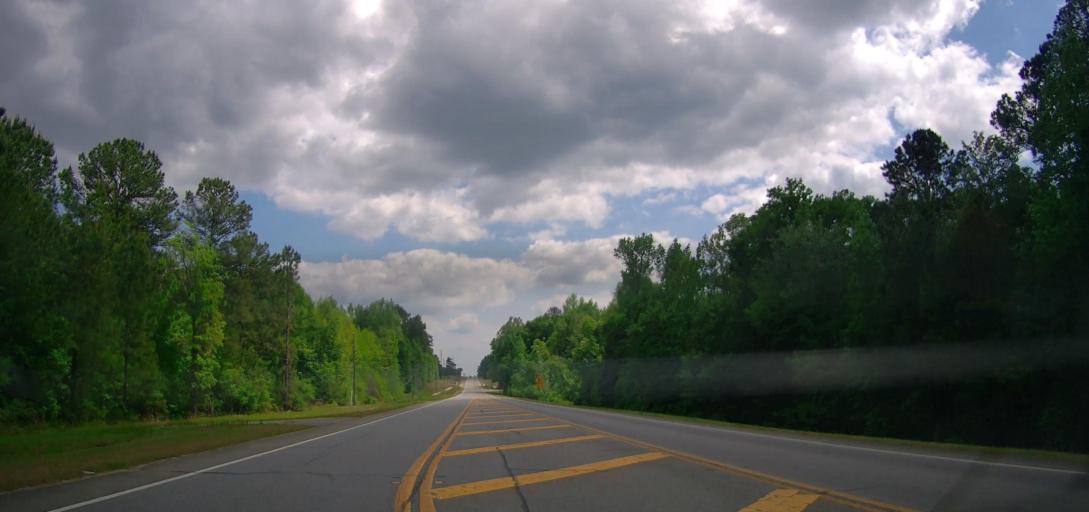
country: US
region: Georgia
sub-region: Laurens County
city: East Dublin
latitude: 32.5160
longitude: -82.8429
